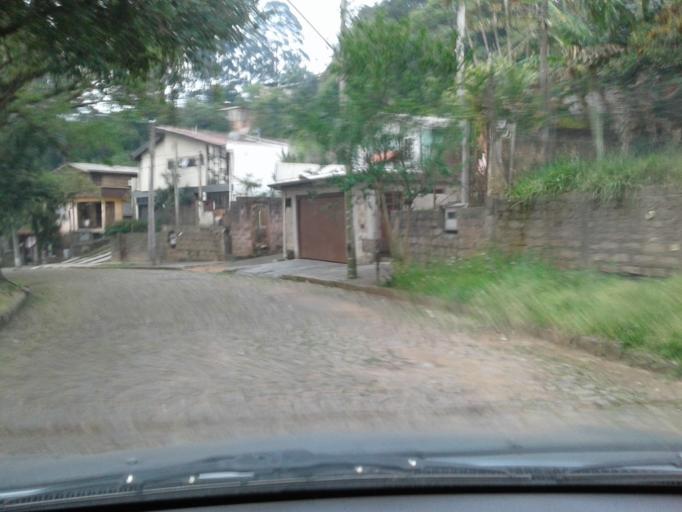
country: BR
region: Rio Grande do Sul
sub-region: Porto Alegre
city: Porto Alegre
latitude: -30.0632
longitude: -51.1475
